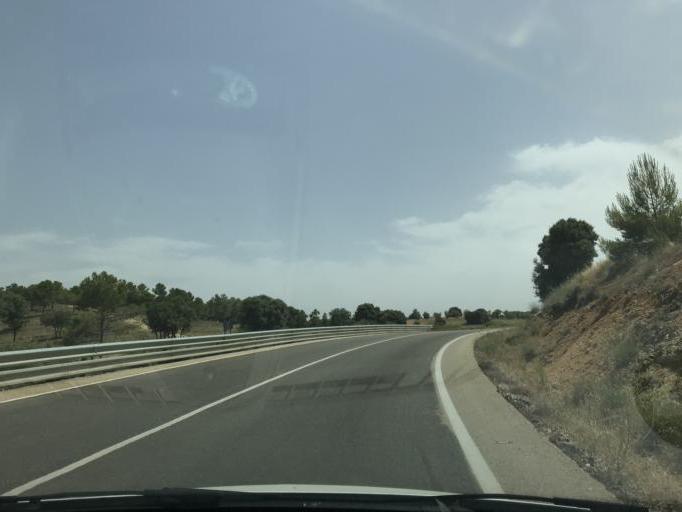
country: ES
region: Castille-La Mancha
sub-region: Provincia de Cuenca
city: Albalate de las Nogueras
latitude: 40.3941
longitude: -2.2624
